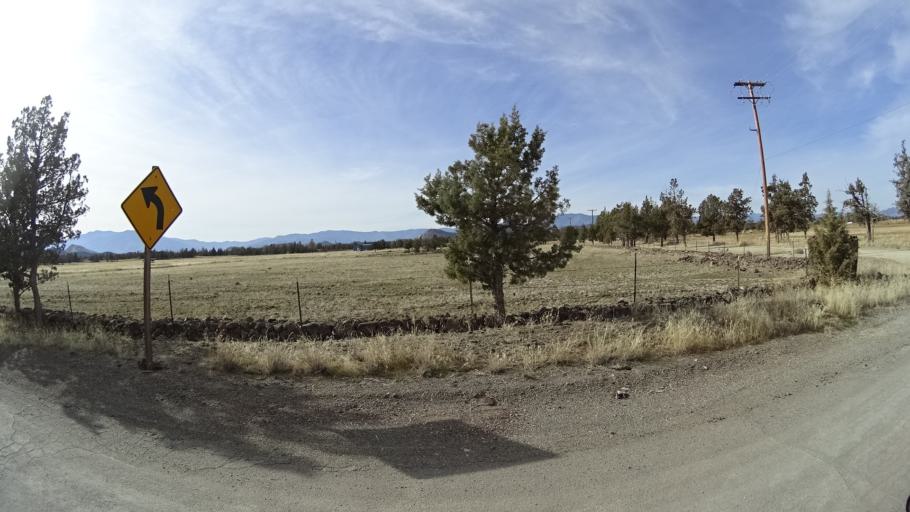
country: US
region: California
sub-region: Siskiyou County
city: Weed
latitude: 41.5953
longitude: -122.4032
